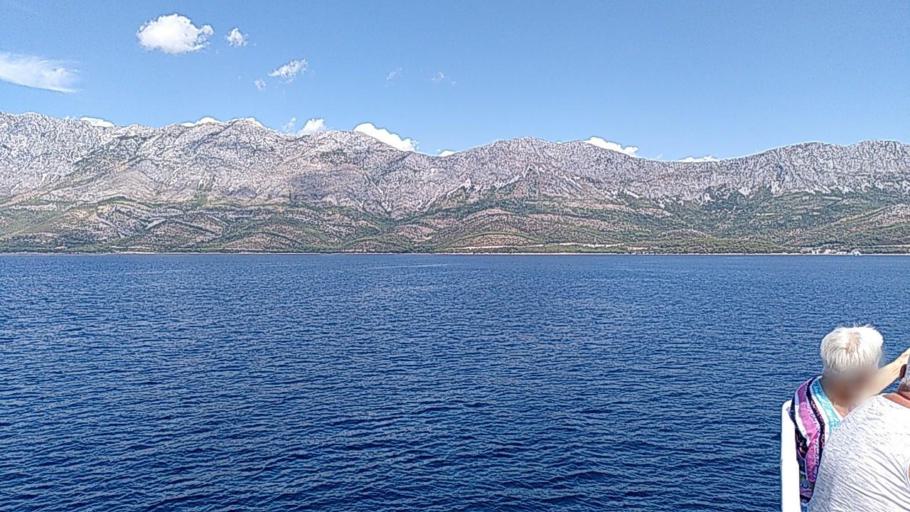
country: HR
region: Dubrovacko-Neretvanska
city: Orebic
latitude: 43.1340
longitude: 17.2169
